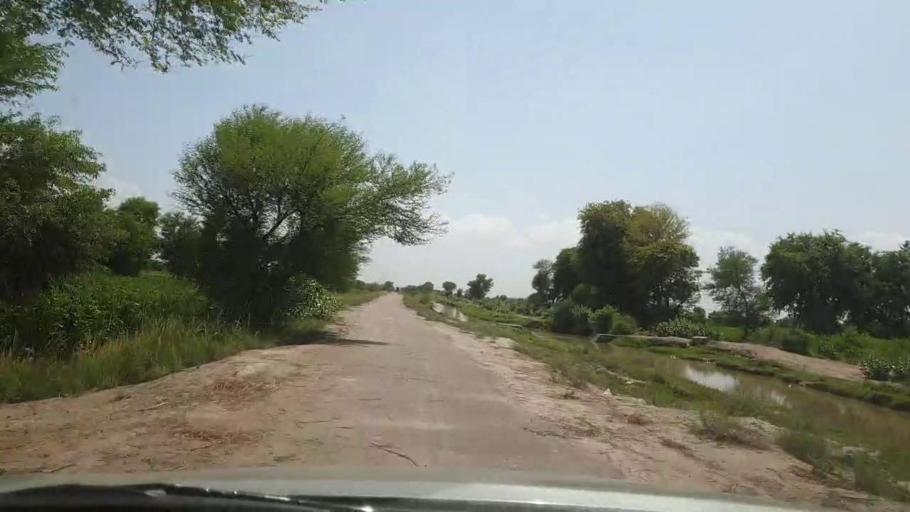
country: PK
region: Sindh
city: Pano Aqil
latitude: 27.7257
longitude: 69.0893
